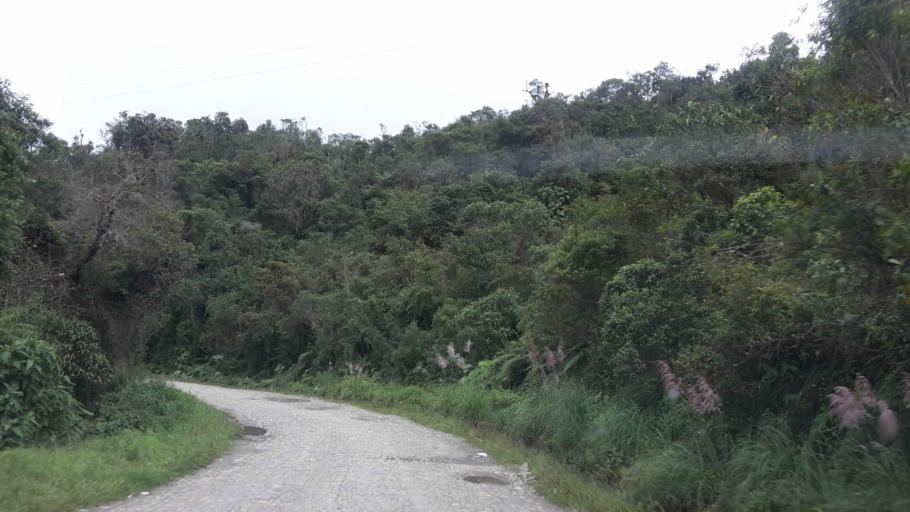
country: BO
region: Cochabamba
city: Colomi
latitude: -17.1608
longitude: -65.9055
